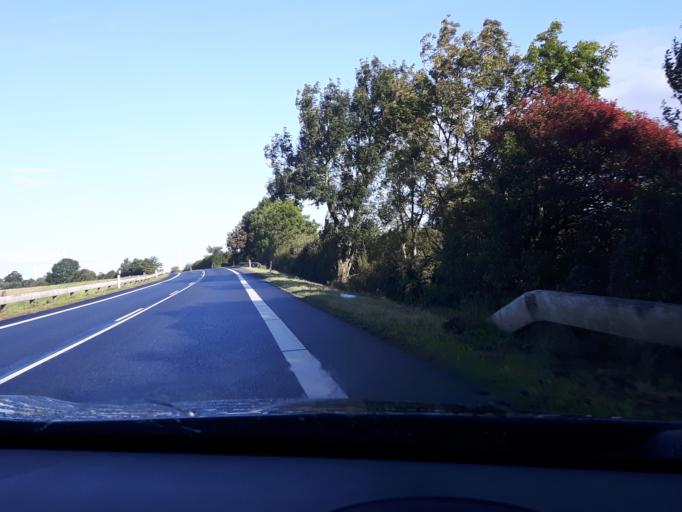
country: DK
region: South Denmark
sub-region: Middelfart Kommune
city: Brenderup
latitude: 55.4484
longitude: 9.9796
